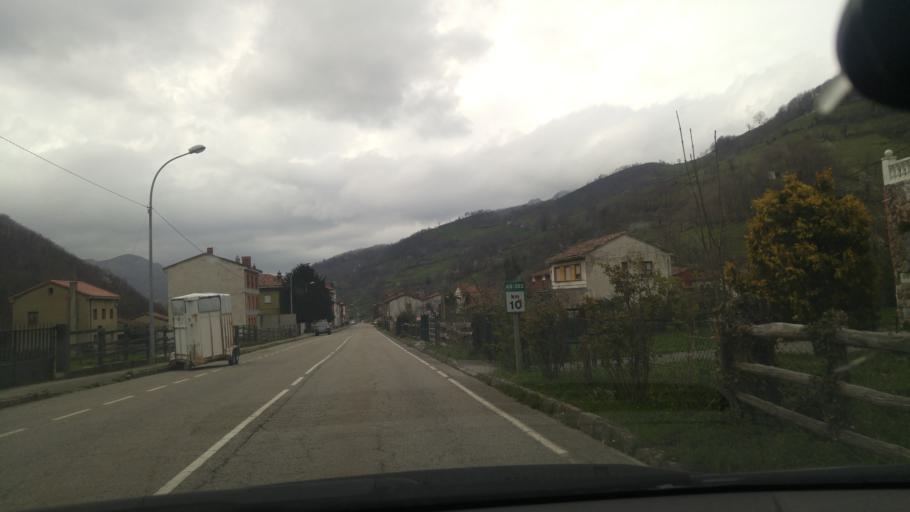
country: ES
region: Asturias
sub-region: Province of Asturias
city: Rio Aller
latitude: 43.1127
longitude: -5.5282
